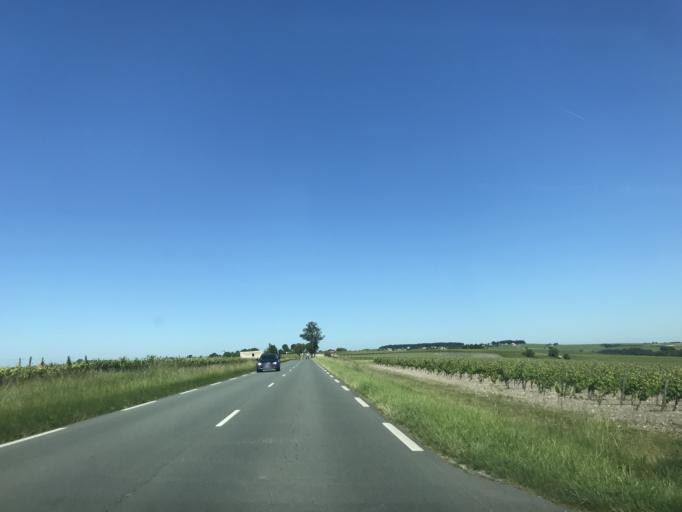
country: FR
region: Poitou-Charentes
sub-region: Departement de la Charente-Maritime
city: Perignac
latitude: 45.5748
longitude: -0.4274
